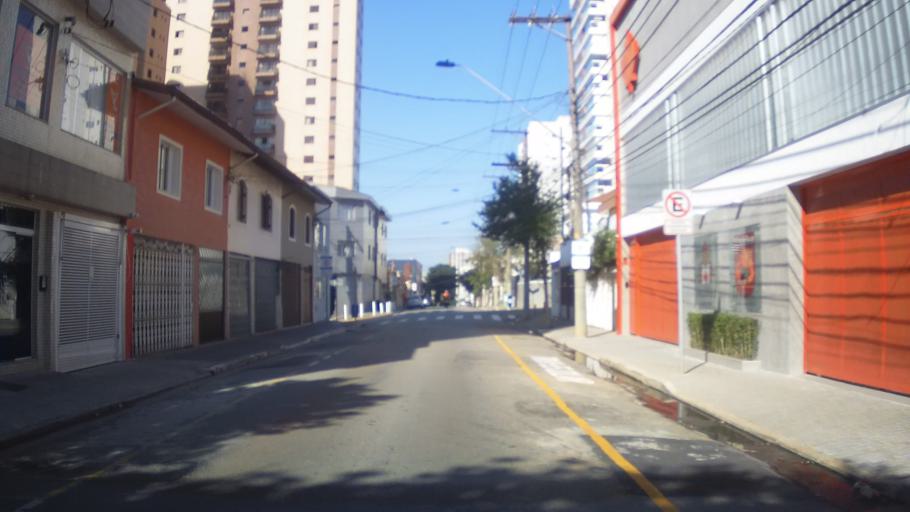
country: BR
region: Sao Paulo
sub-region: Sao Caetano Do Sul
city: Sao Caetano do Sul
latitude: -23.6174
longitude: -46.5633
